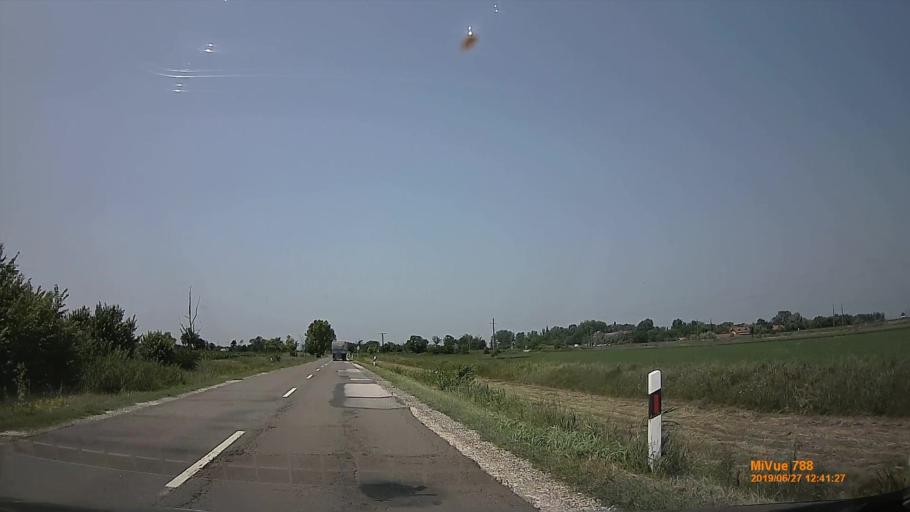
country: HU
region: Pest
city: Tortel
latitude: 47.1806
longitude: 19.8970
